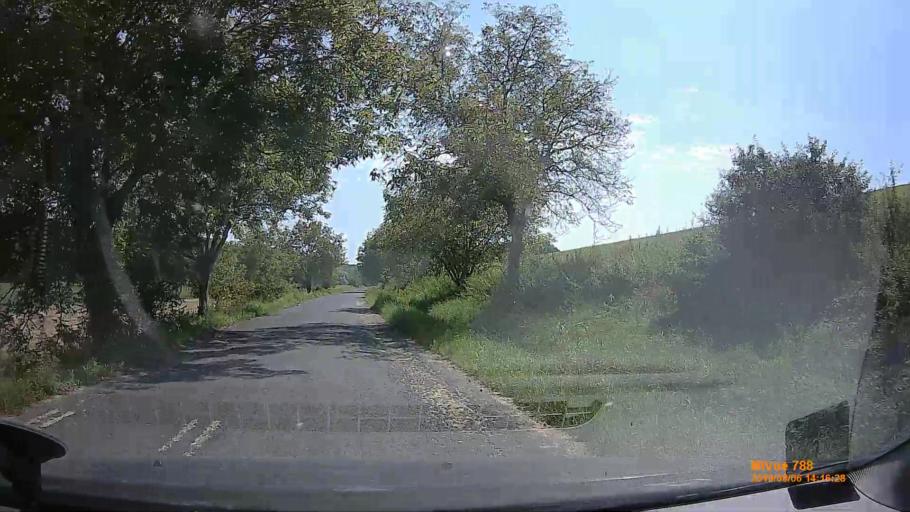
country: HU
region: Zala
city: Zalakomar
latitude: 46.5528
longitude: 17.0809
